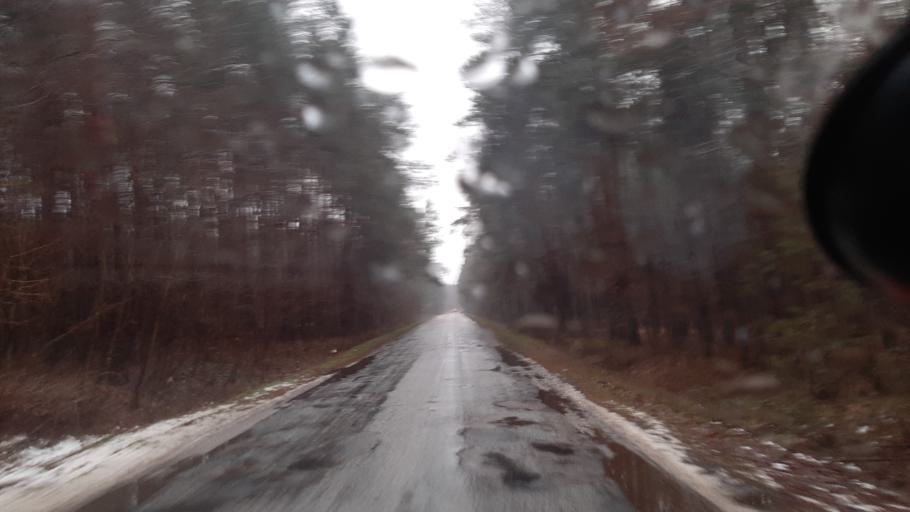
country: PL
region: Lublin Voivodeship
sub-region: Powiat lubartowski
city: Firlej
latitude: 51.5178
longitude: 22.4963
